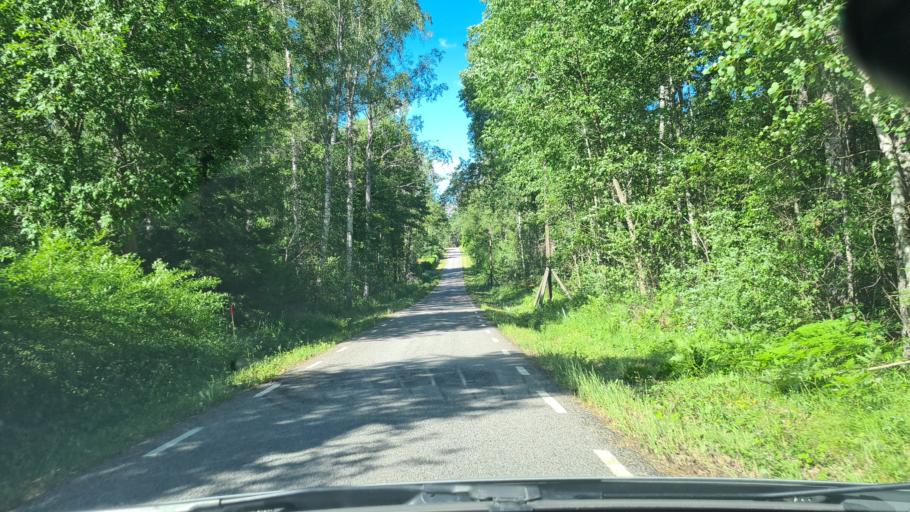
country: SE
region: OEstergoetland
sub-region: Norrkopings Kommun
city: Krokek
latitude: 58.7166
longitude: 16.4283
